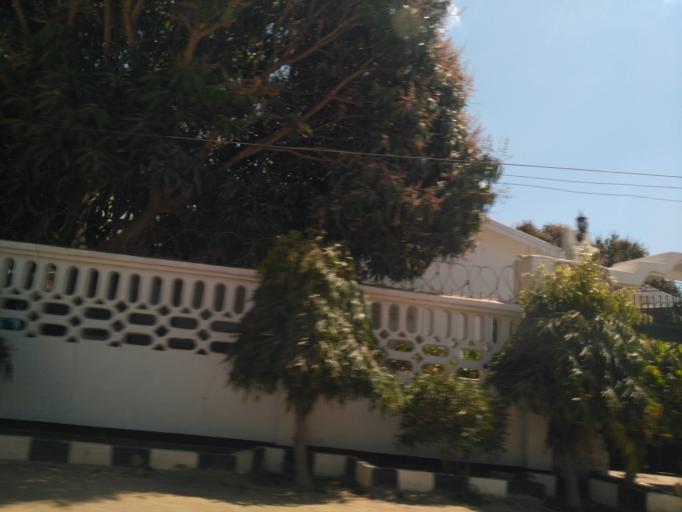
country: TZ
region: Dodoma
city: Dodoma
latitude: -6.1680
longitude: 35.7602
